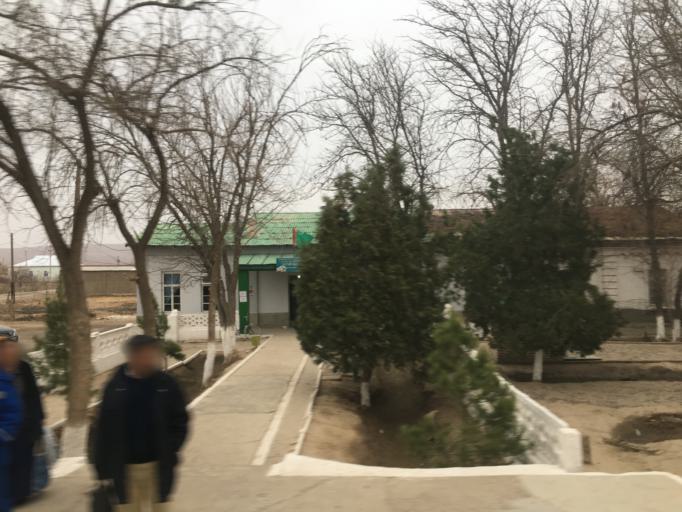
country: TM
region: Mary
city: Yoloeten
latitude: 36.5383
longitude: 62.5539
